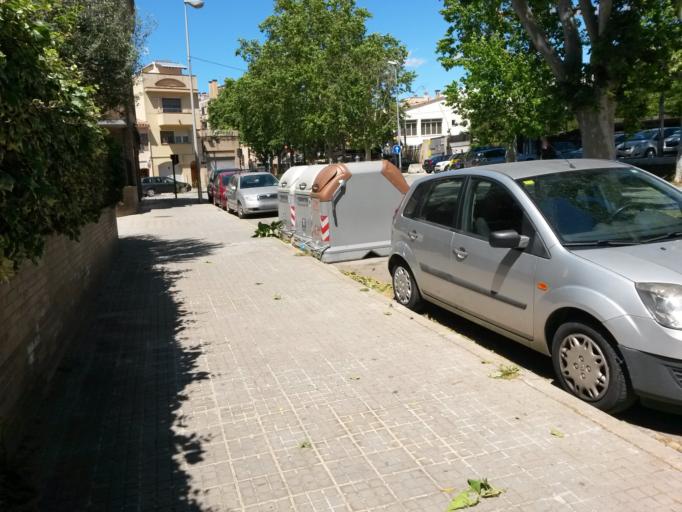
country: ES
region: Catalonia
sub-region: Provincia de Barcelona
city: Cerdanyola del Valles
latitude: 41.4881
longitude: 2.1319
